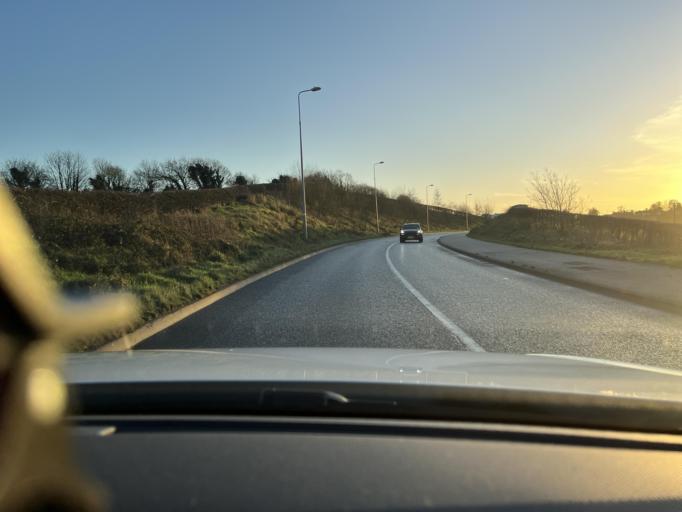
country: IE
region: Ulster
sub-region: An Cabhan
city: Ballyconnell
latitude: 54.1190
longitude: -7.5726
